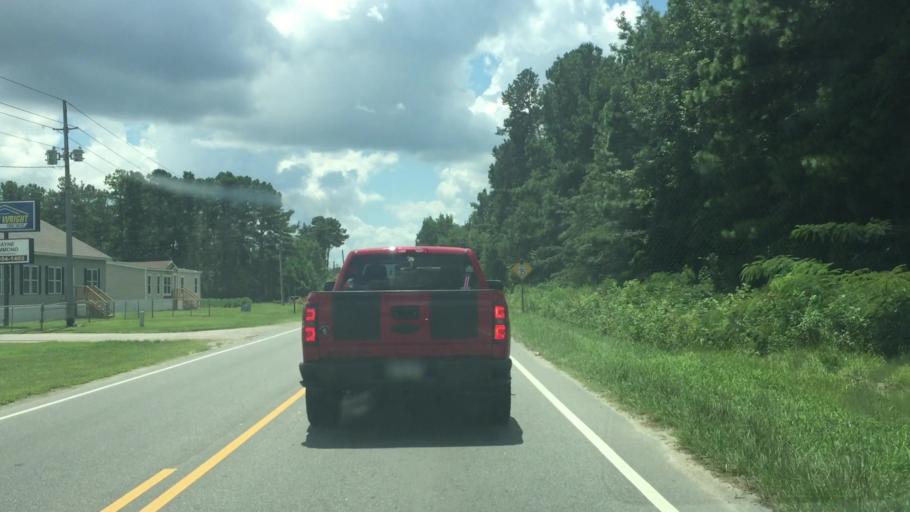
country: US
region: North Carolina
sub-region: Columbus County
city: Chadbourn
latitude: 34.3375
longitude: -78.8271
